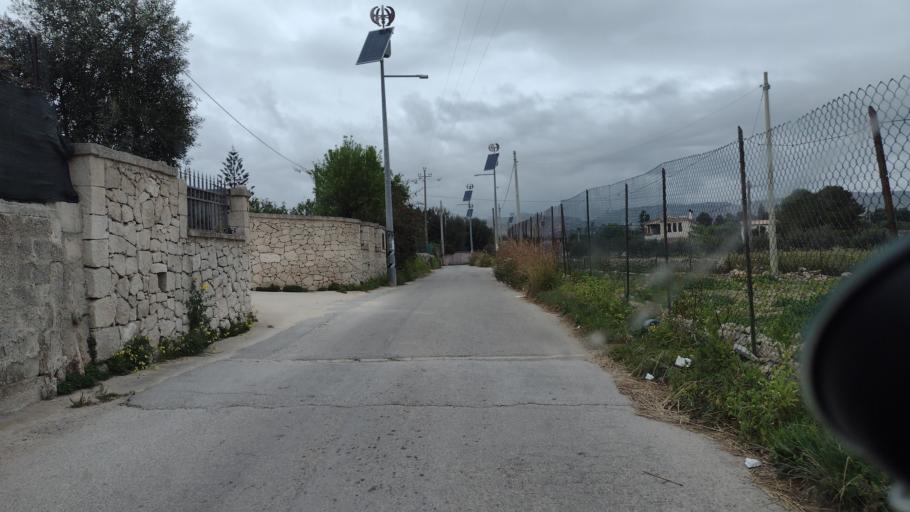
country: IT
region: Sicily
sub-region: Provincia di Siracusa
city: Avola
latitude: 36.8934
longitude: 15.1160
